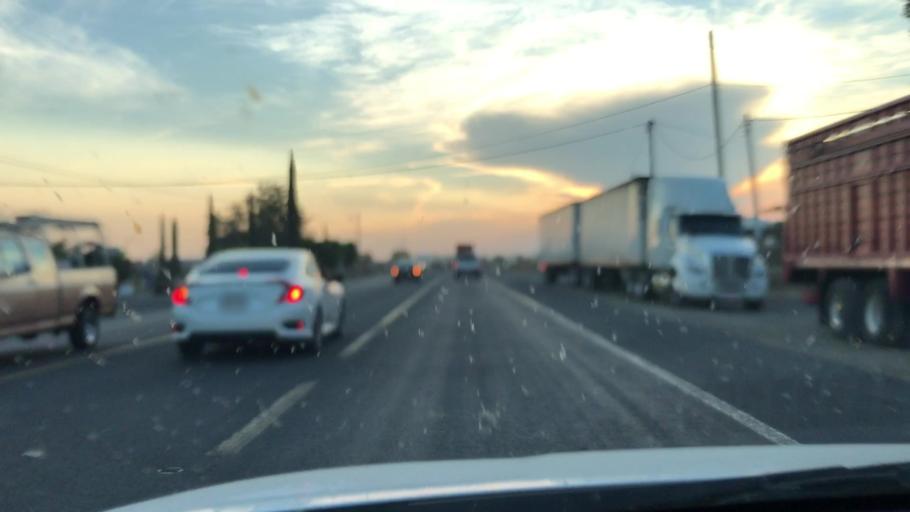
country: MX
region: Michoacan
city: Tanhuato de Guerrero
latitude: 20.3000
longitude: -102.3244
